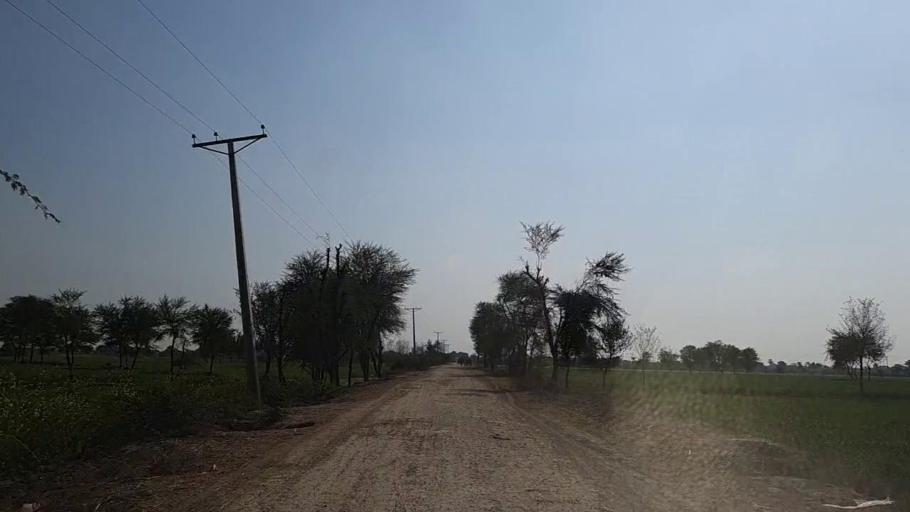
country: PK
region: Sindh
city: Daur
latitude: 26.4562
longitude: 68.2348
